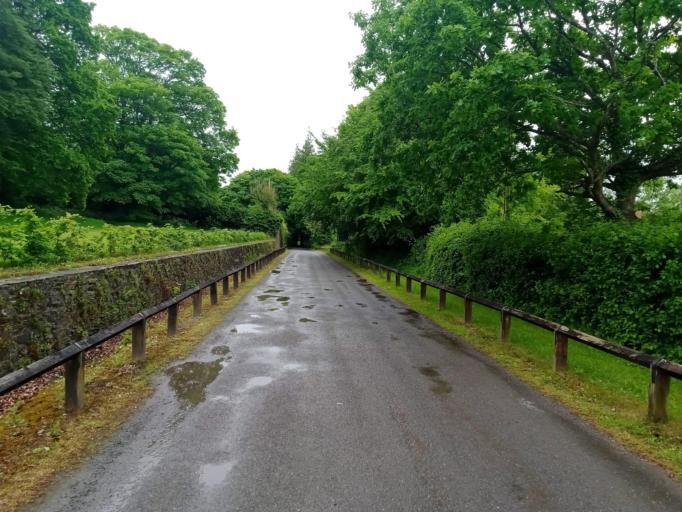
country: IE
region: Leinster
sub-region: Kilkenny
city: Thomastown
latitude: 52.4767
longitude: -7.0578
